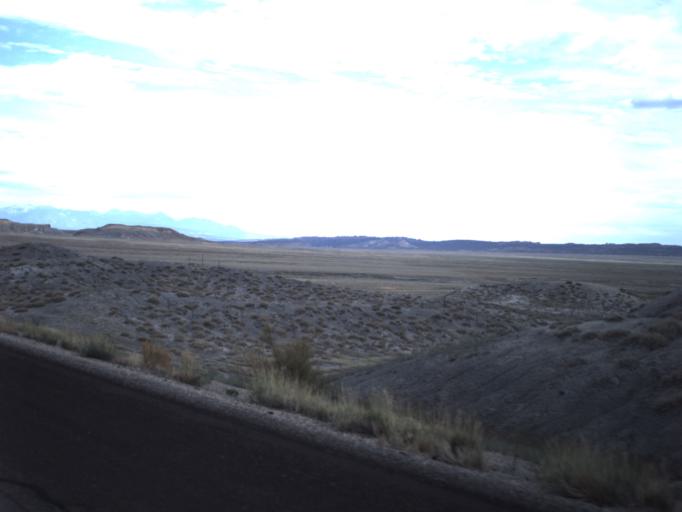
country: US
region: Utah
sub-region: Grand County
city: Moab
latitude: 38.9541
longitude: -109.7036
